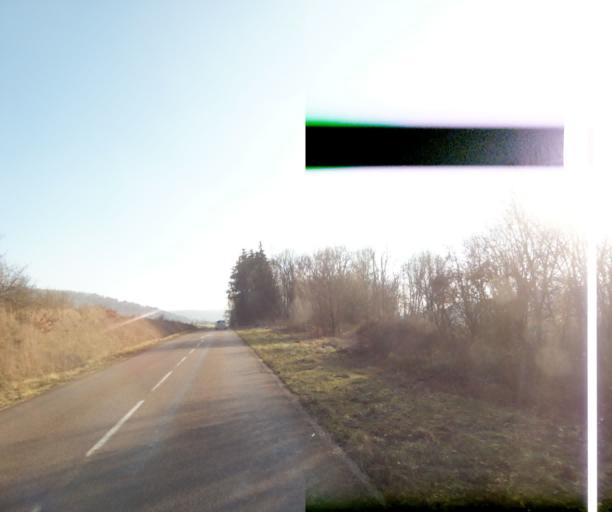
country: FR
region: Champagne-Ardenne
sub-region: Departement de la Haute-Marne
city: Chevillon
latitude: 48.5019
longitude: 5.1281
